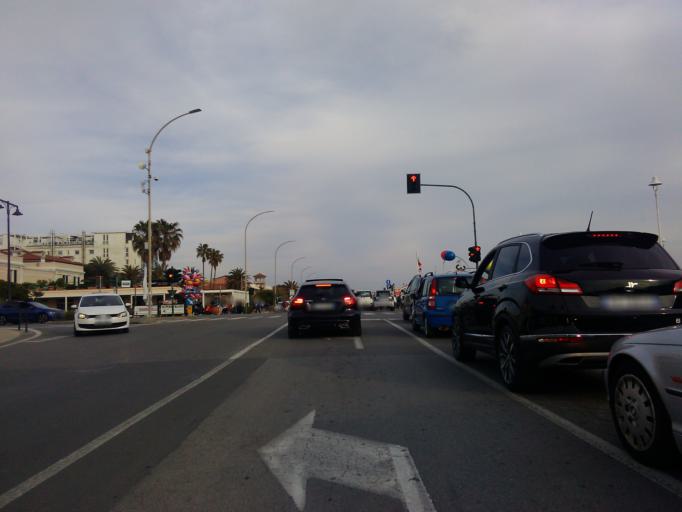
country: IT
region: Tuscany
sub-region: Provincia di Massa-Carrara
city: Massa
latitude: 44.0081
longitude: 10.0986
